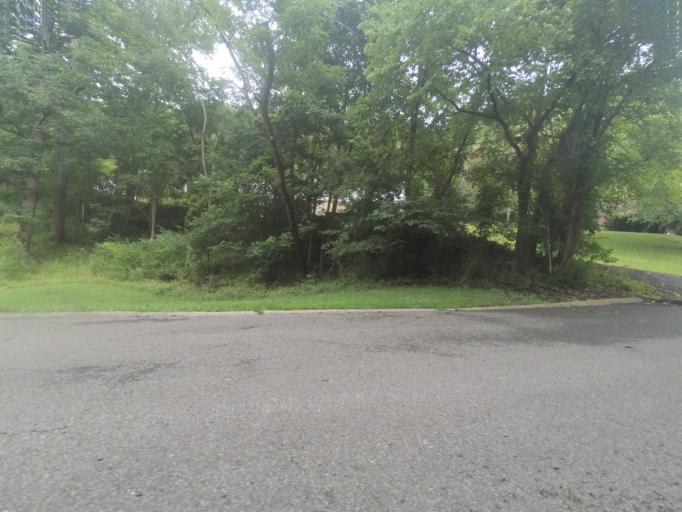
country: US
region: West Virginia
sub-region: Cabell County
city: Huntington
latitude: 38.3959
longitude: -82.4034
